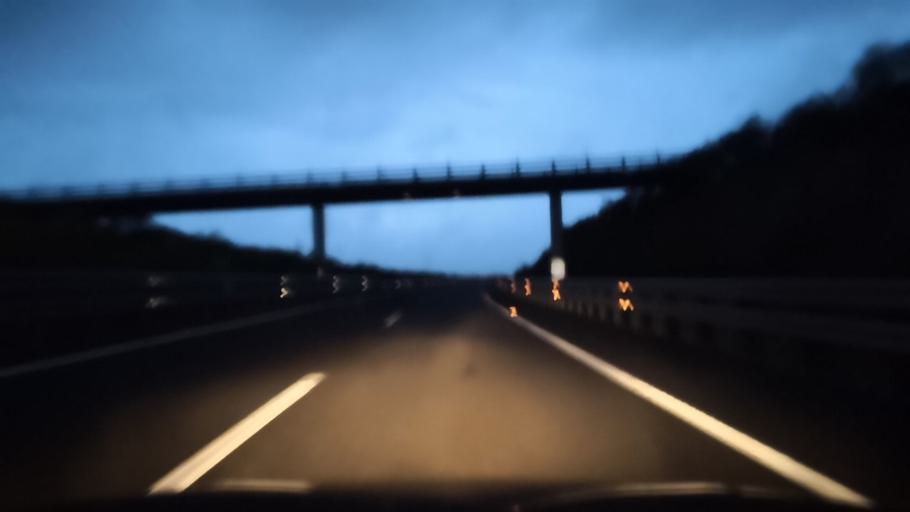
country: ES
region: Extremadura
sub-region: Provincia de Caceres
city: Aldea del Cano
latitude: 39.3451
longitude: -6.3424
